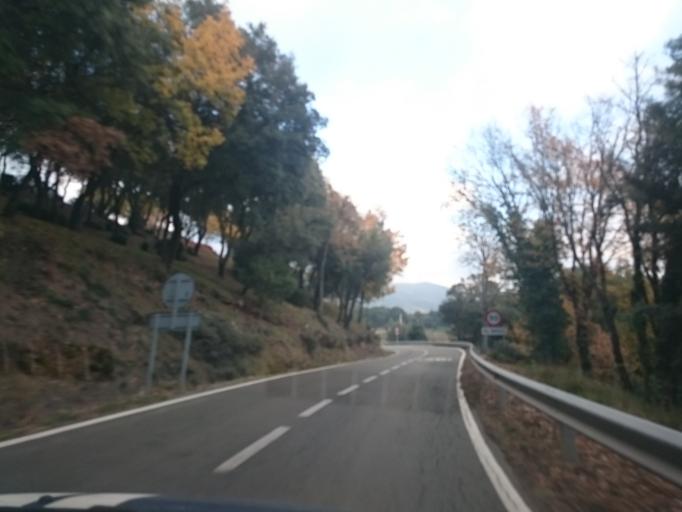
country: ES
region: Catalonia
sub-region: Provincia de Barcelona
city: Seva
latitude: 41.8166
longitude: 2.3036
